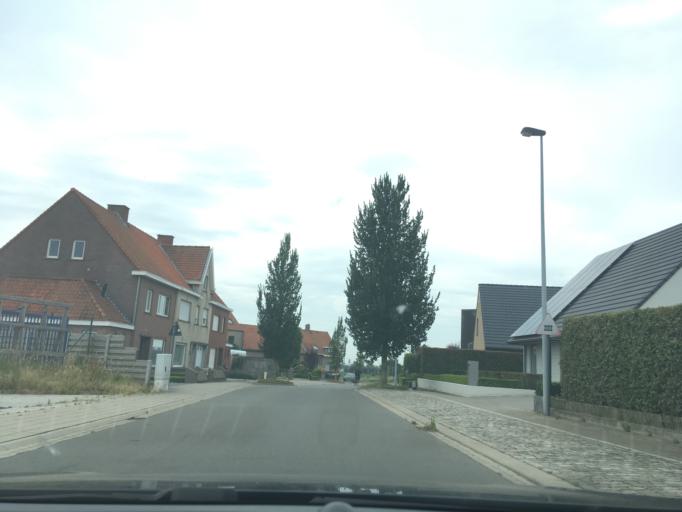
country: BE
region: Flanders
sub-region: Provincie West-Vlaanderen
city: Tielt
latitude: 50.9878
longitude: 3.3228
